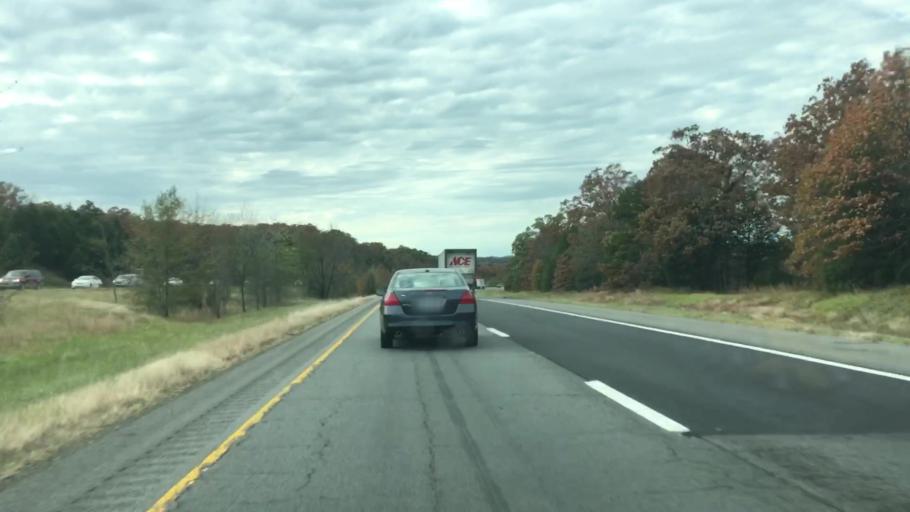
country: US
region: Arkansas
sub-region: Faulkner County
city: Conway
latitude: 35.1231
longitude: -92.5020
